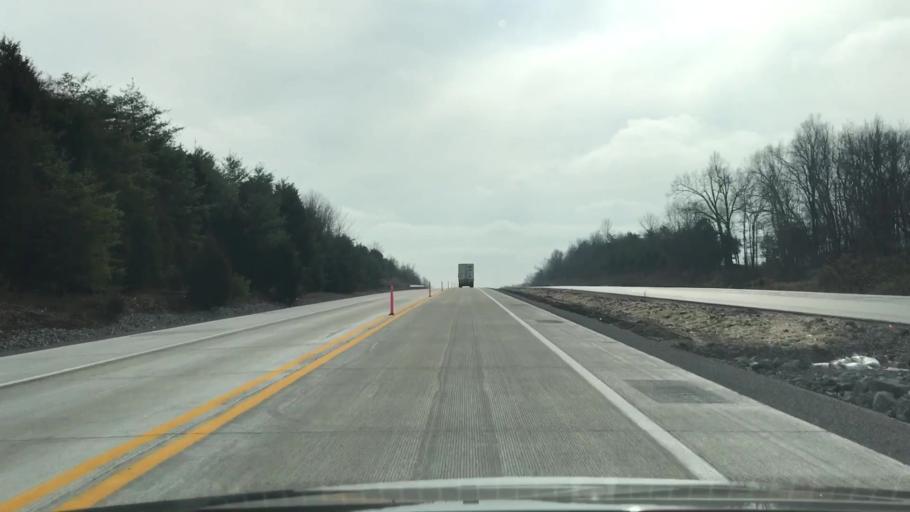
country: US
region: Kentucky
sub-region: Christian County
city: Hopkinsville
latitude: 36.9720
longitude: -87.4652
